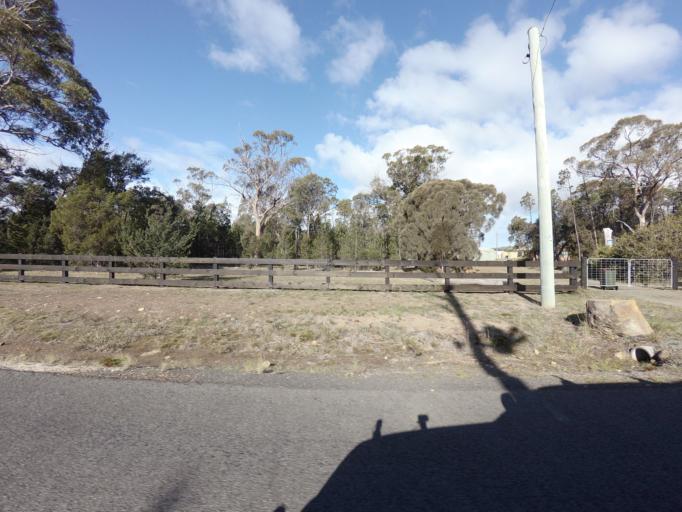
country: AU
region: Tasmania
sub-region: Sorell
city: Sorell
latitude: -42.3042
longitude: 147.9919
